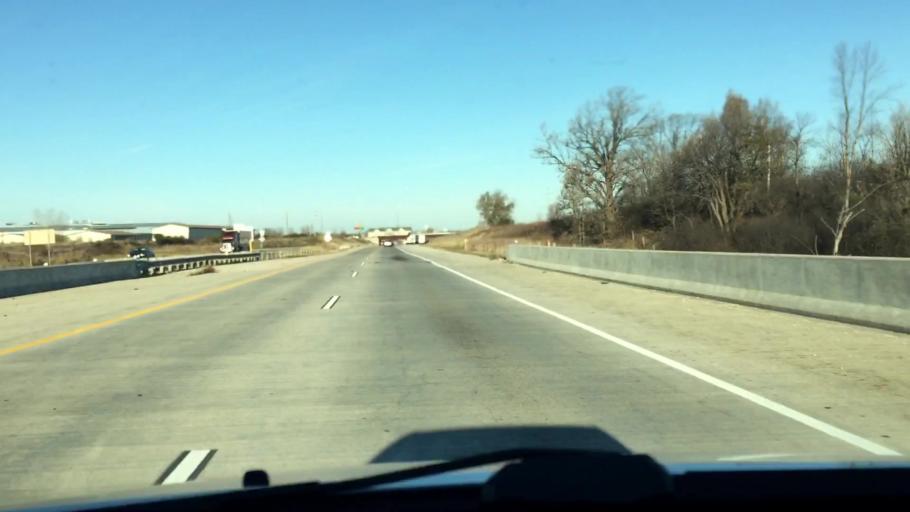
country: US
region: Wisconsin
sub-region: Fond du Lac County
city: Fond du Lac
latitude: 43.7456
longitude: -88.4536
